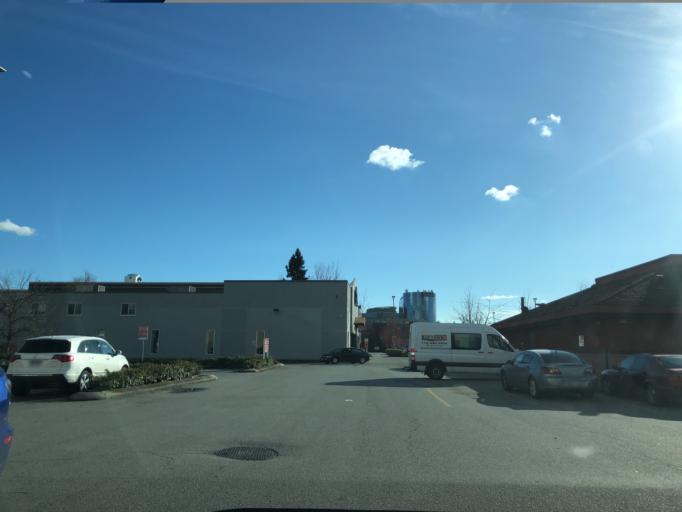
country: CA
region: British Columbia
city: Richmond
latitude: 49.1876
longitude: -123.1328
